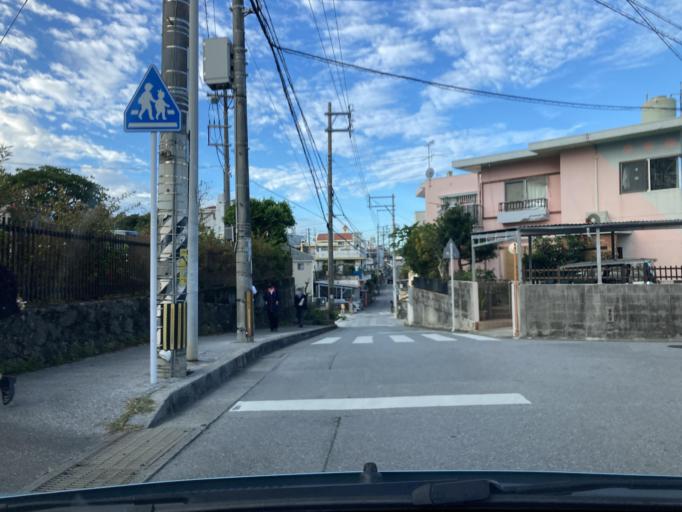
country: JP
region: Okinawa
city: Naha-shi
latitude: 26.2302
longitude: 127.7246
